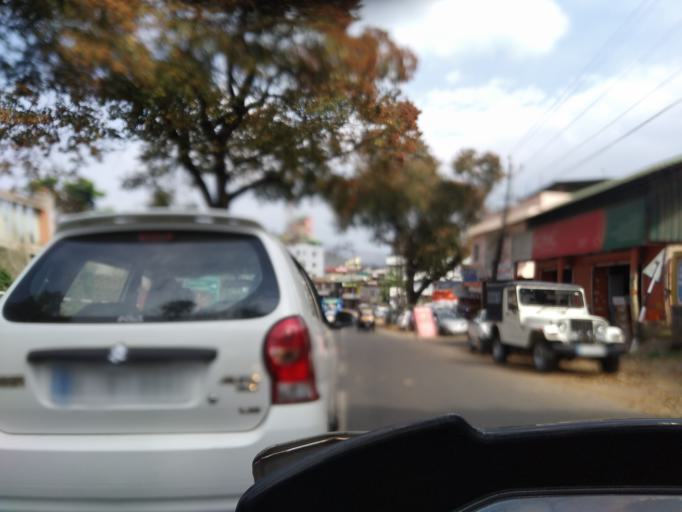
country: IN
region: Tamil Nadu
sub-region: Theni
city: Gudalur
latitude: 9.6090
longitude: 77.1670
